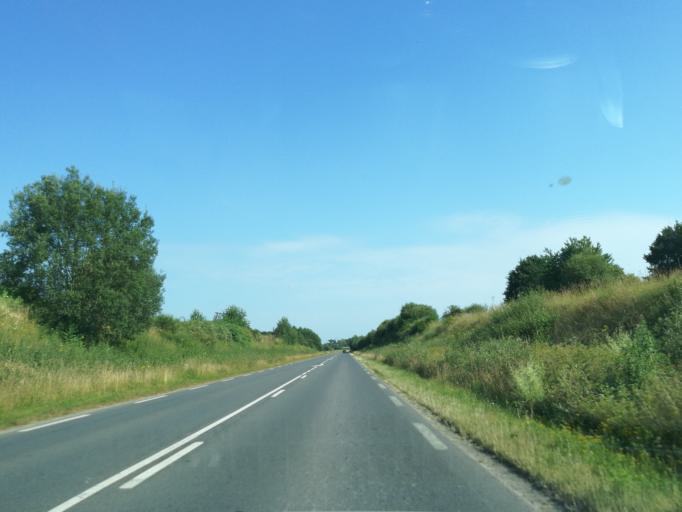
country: FR
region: Brittany
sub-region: Departement d'Ille-et-Vilaine
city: Montfort-sur-Meu
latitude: 48.1408
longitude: -1.9379
